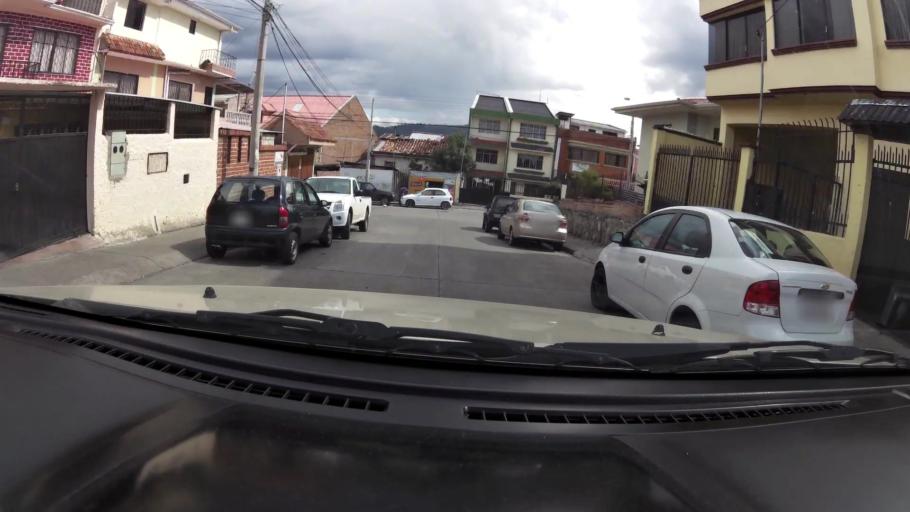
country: EC
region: Azuay
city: Cuenca
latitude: -2.8896
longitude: -78.9963
